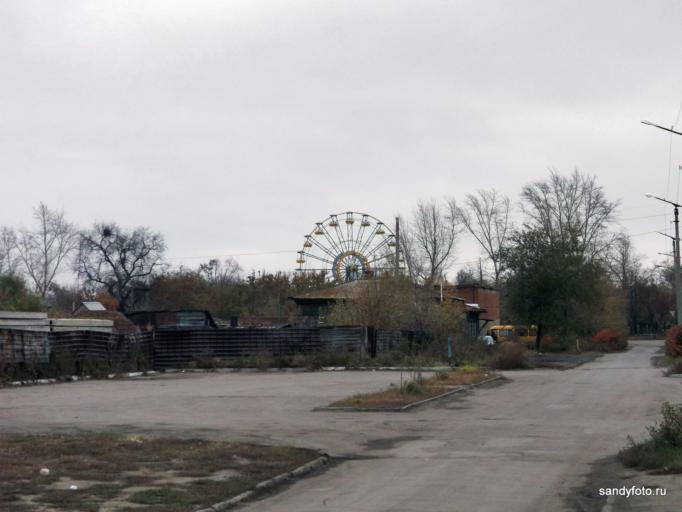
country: RU
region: Chelyabinsk
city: Troitsk
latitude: 54.0875
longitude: 61.5492
